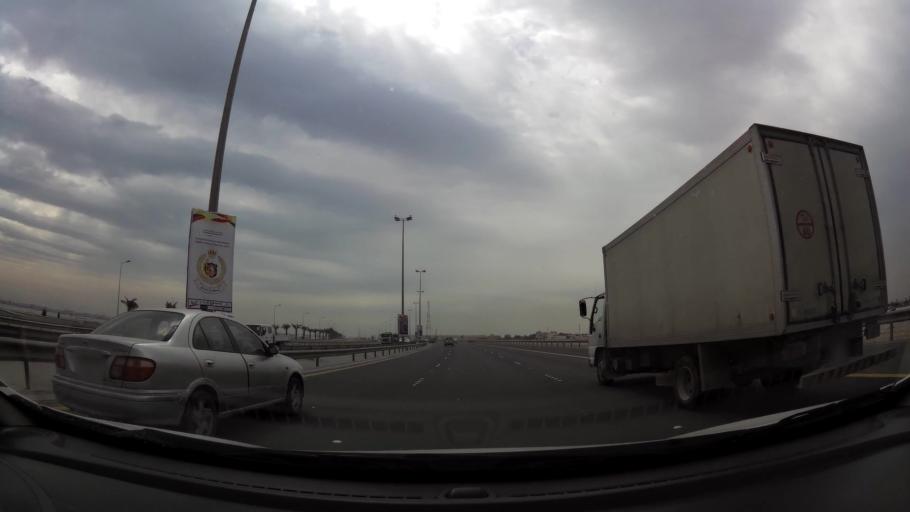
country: BH
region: Manama
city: Manama
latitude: 26.1909
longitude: 50.5885
